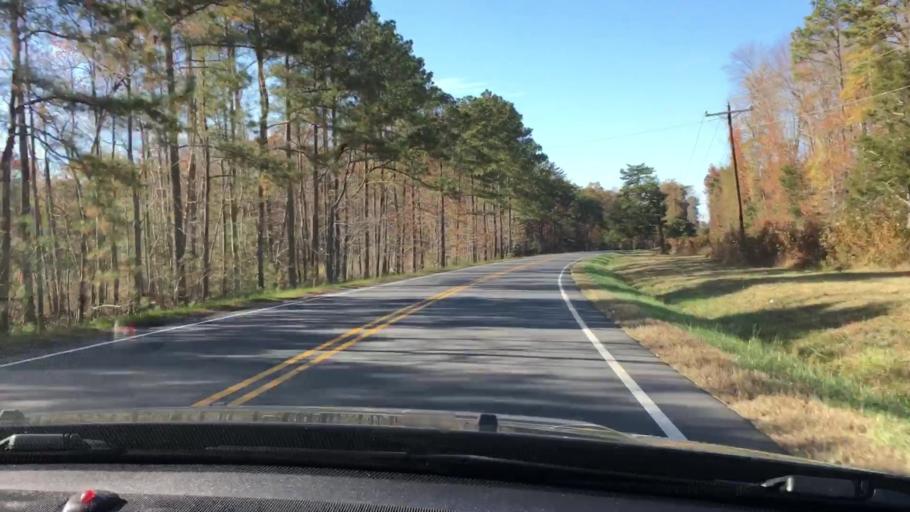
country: US
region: Virginia
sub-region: King William County
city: King William
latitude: 37.6766
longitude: -76.9973
